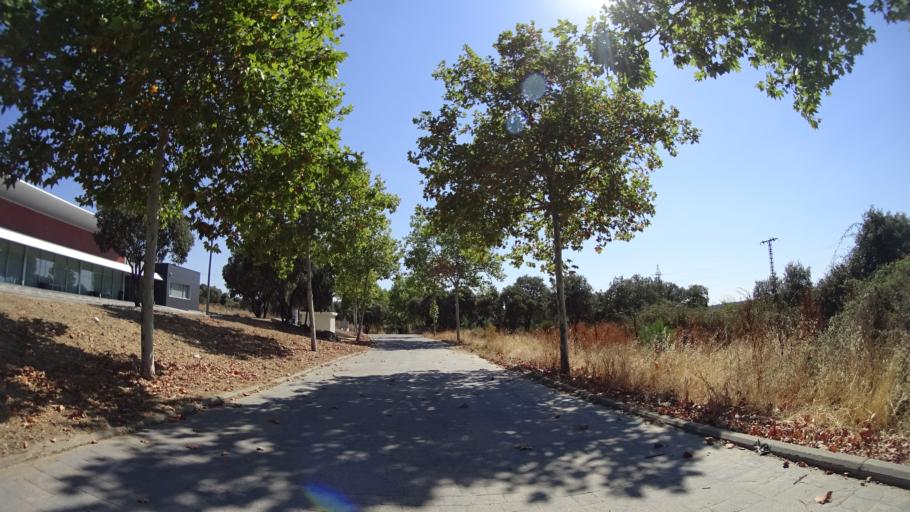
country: ES
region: Madrid
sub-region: Provincia de Madrid
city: Galapagar
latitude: 40.5982
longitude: -4.0112
